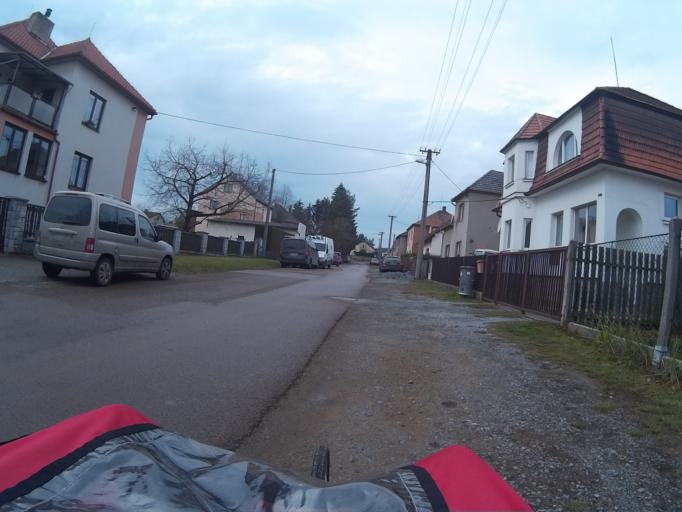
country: CZ
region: Plzensky
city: St'ahlavy
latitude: 49.6699
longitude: 13.4987
